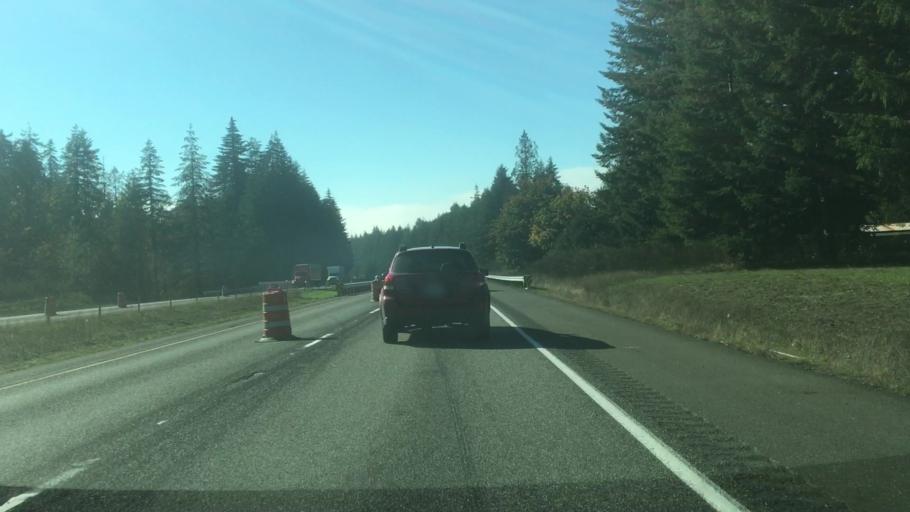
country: US
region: Washington
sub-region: Grays Harbor County
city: McCleary
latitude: 47.0494
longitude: -123.3049
